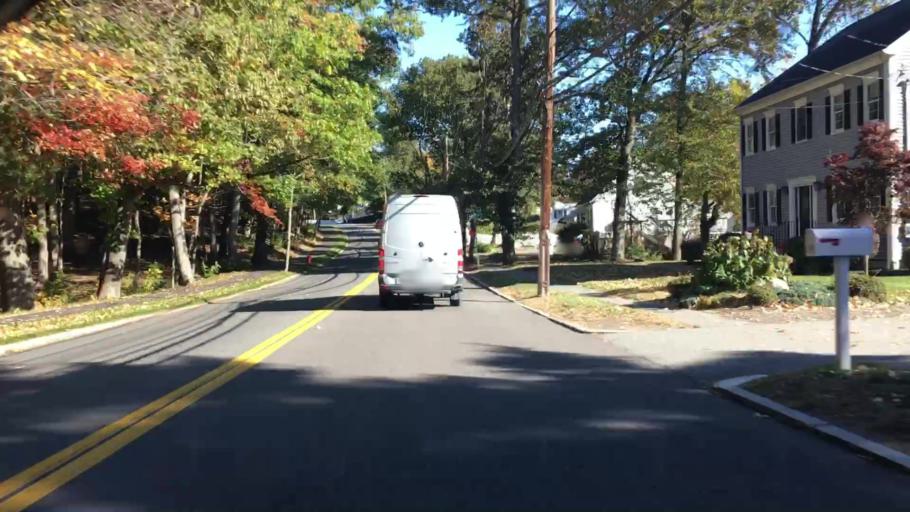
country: US
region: Massachusetts
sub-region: Middlesex County
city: Lexington
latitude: 42.4169
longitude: -71.2524
